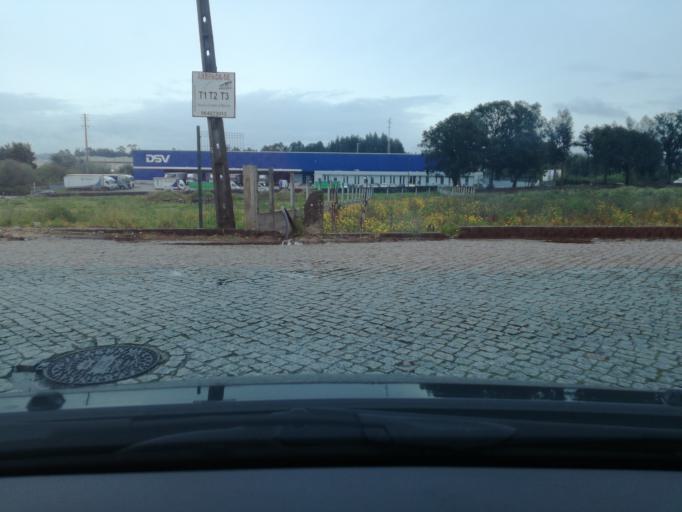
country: PT
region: Porto
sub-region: Maia
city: Gemunde
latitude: 41.2602
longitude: -8.6632
